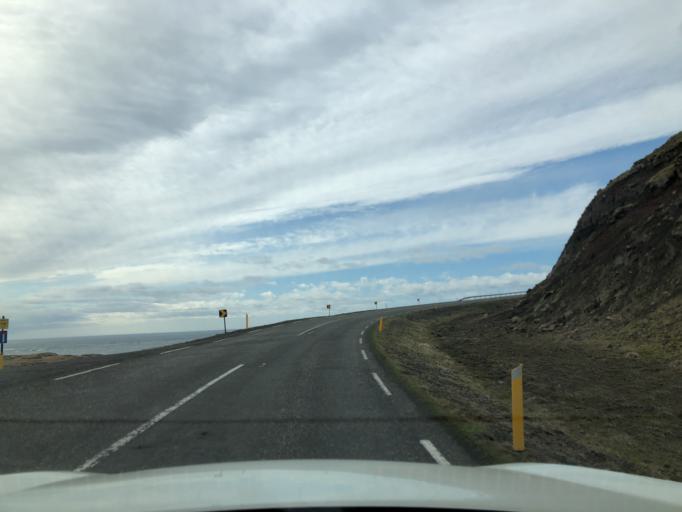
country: IS
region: East
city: Eskifjoerdur
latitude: 64.8069
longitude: -13.8626
